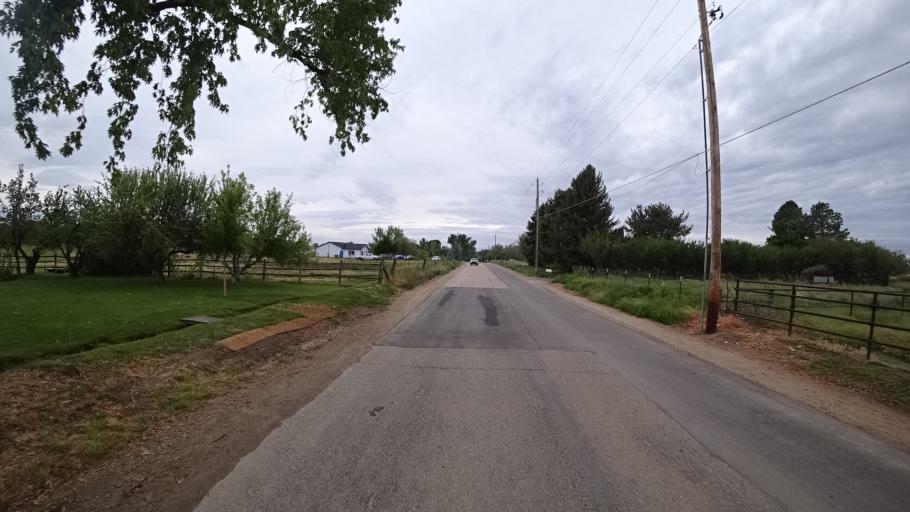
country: US
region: Idaho
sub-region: Ada County
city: Star
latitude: 43.7129
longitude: -116.4883
